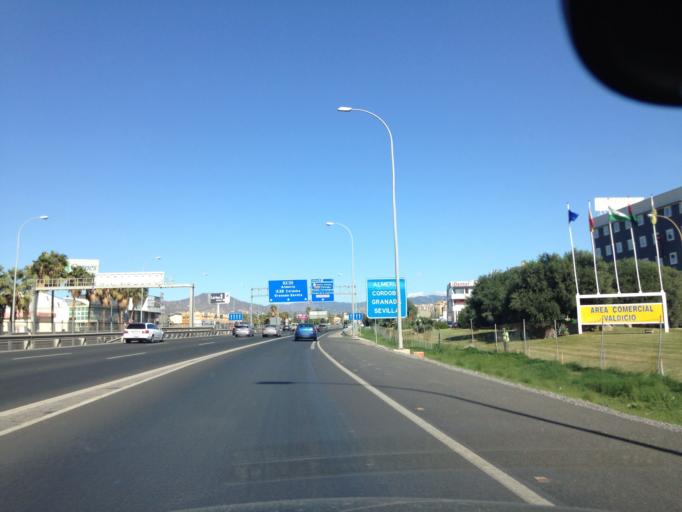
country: ES
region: Andalusia
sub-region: Provincia de Malaga
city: Malaga
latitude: 36.6904
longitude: -4.4615
